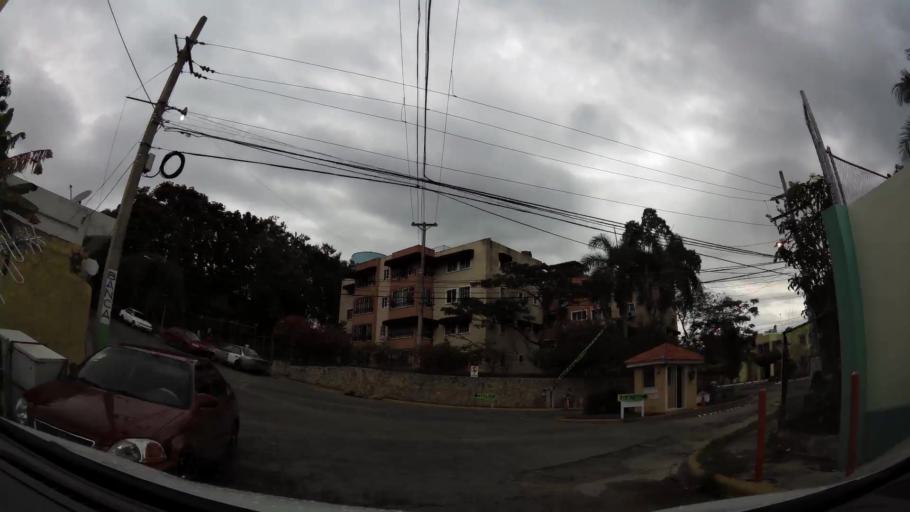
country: DO
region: Nacional
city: La Agustina
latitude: 18.5064
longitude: -69.9349
